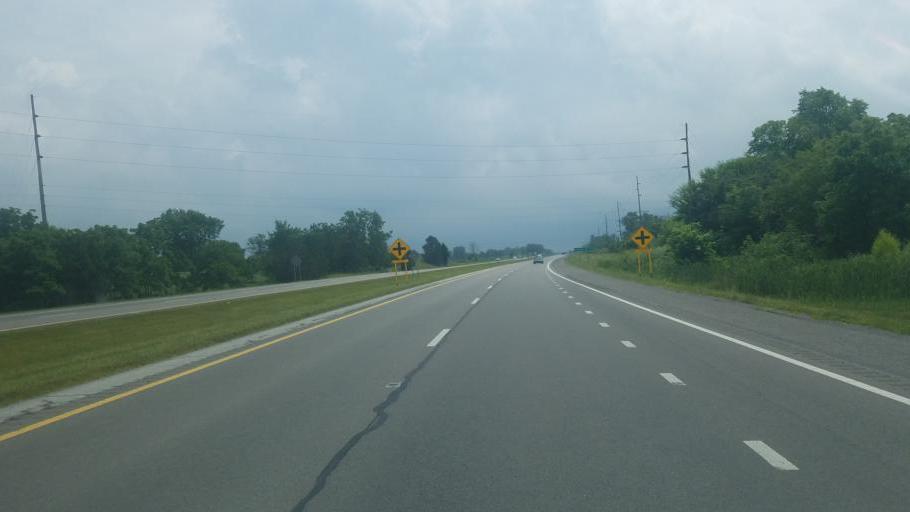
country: US
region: Ohio
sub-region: Logan County
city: Northwood
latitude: 40.4317
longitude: -83.8029
